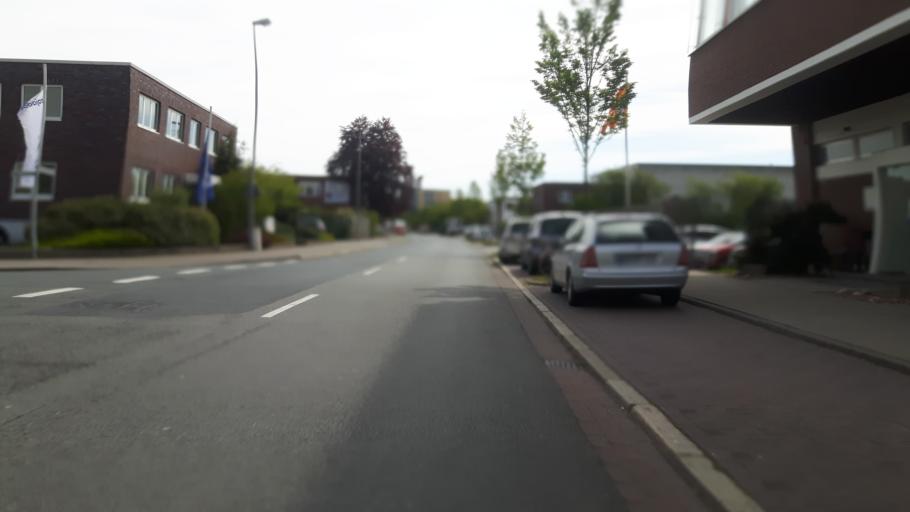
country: DE
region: Lower Saxony
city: Stuhr
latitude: 53.0597
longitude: 8.7734
